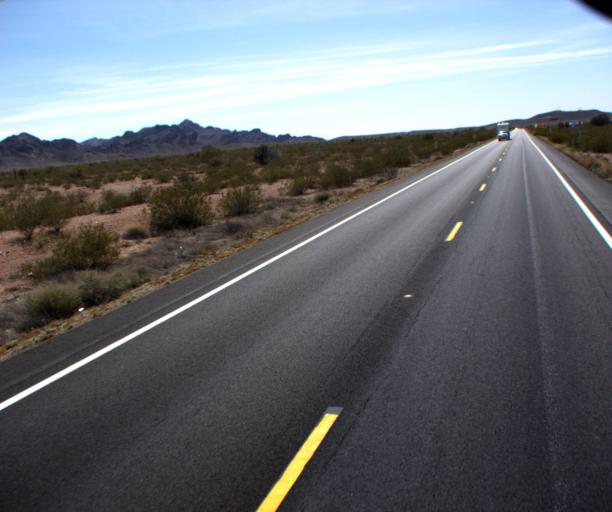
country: US
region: Arizona
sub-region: La Paz County
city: Quartzsite
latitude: 33.2715
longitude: -114.2366
